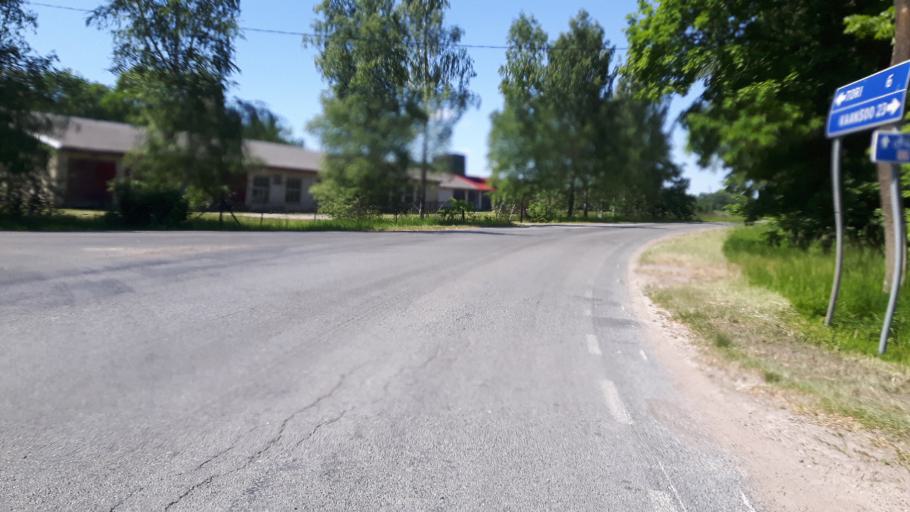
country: EE
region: Paernumaa
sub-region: Tootsi vald
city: Tootsi
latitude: 58.4925
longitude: 24.8967
